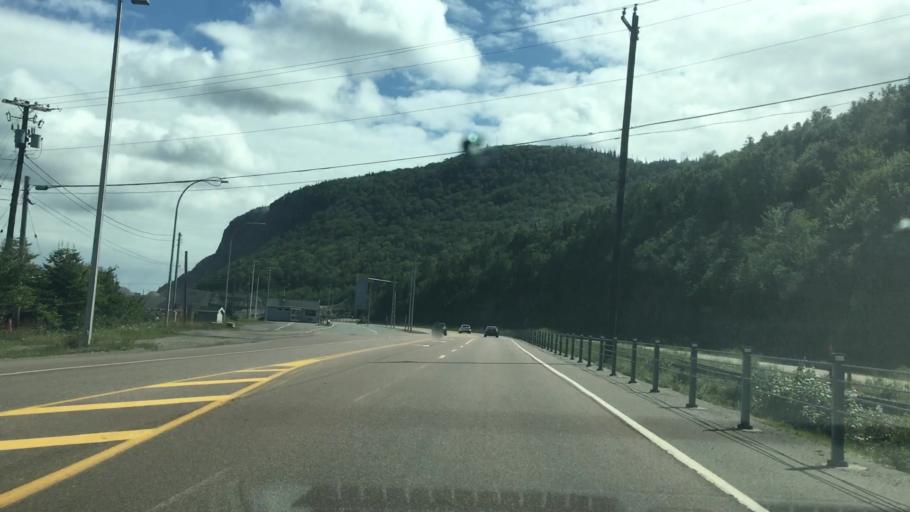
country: CA
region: Nova Scotia
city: Port Hawkesbury
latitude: 45.6429
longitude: -61.4309
